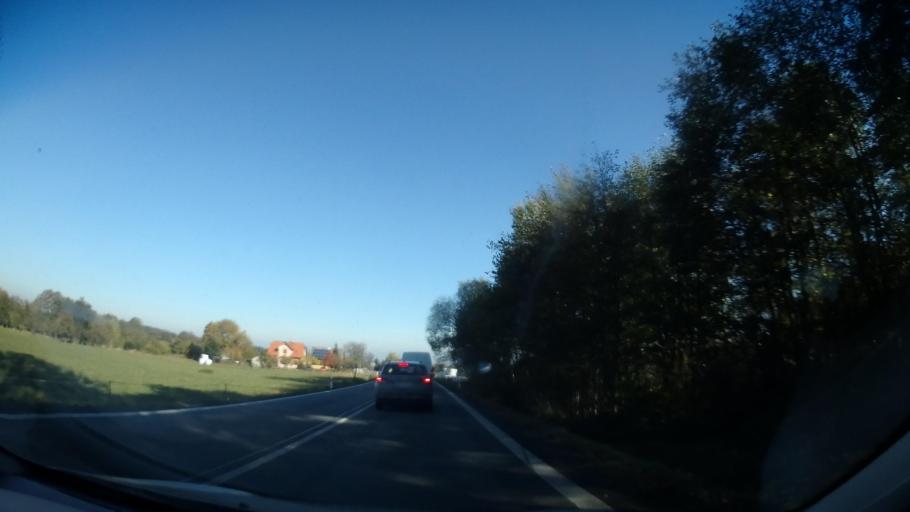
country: CZ
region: Pardubicky
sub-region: Okres Chrudim
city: Nasavrky
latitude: 49.8235
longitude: 15.8190
